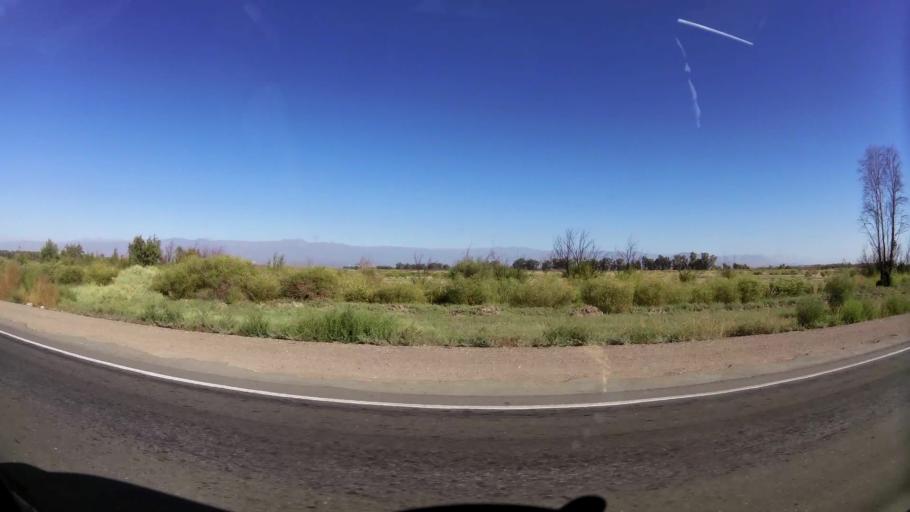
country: AR
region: Mendoza
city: General Lavalle
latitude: -32.7149
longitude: -68.6795
